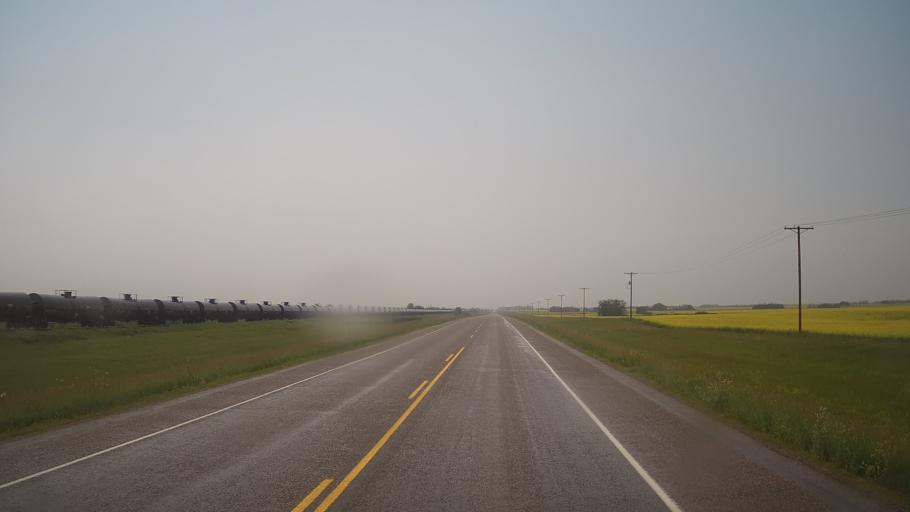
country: CA
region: Saskatchewan
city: Biggar
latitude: 52.1606
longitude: -108.2782
